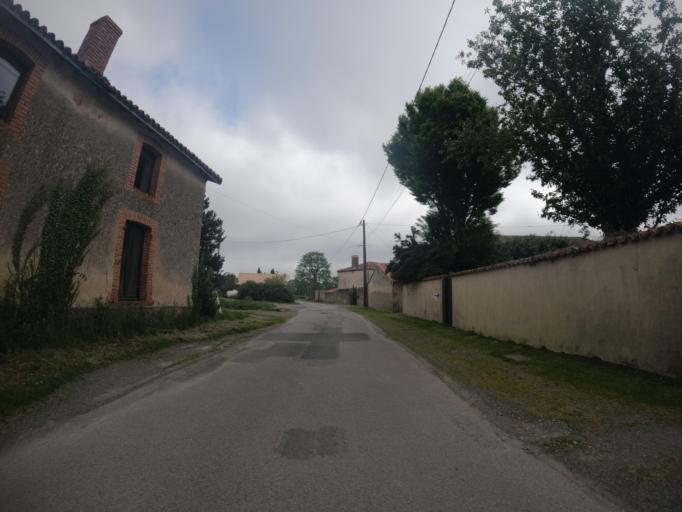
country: FR
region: Poitou-Charentes
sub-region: Departement des Deux-Sevres
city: Chiche
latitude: 46.8178
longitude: -0.3713
